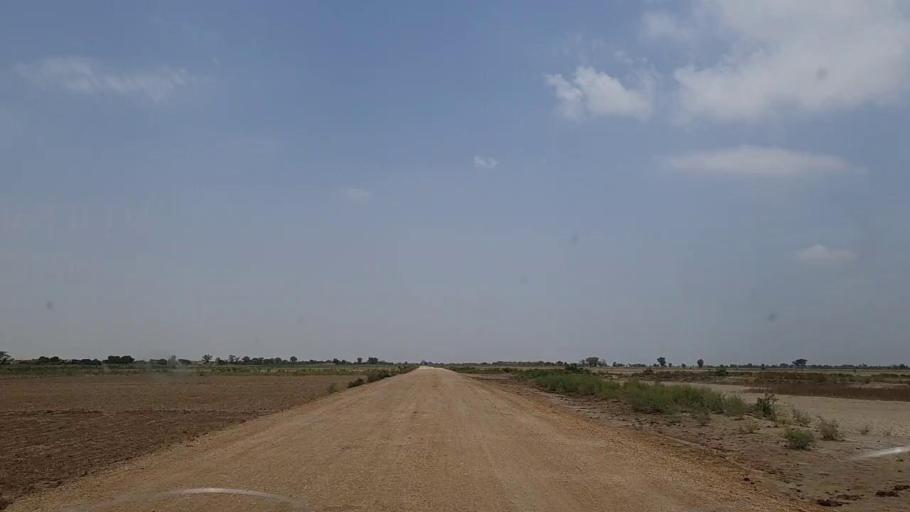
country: PK
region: Sindh
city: Phulji
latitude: 26.8085
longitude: 67.6340
